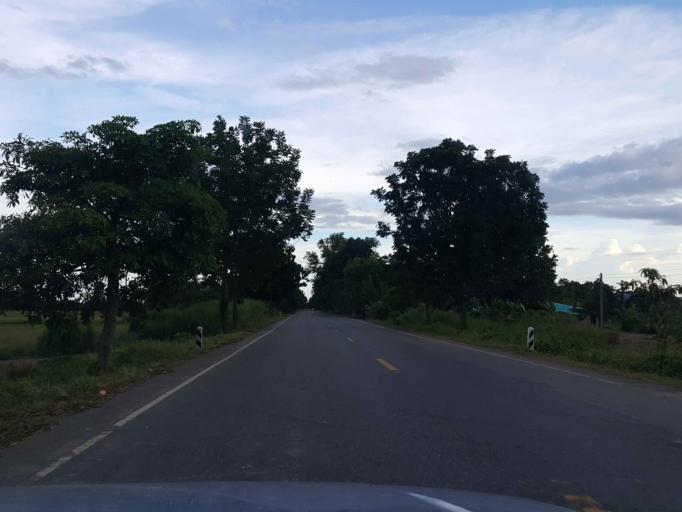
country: TH
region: Sukhothai
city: Sawankhalok
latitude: 17.3508
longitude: 99.7425
